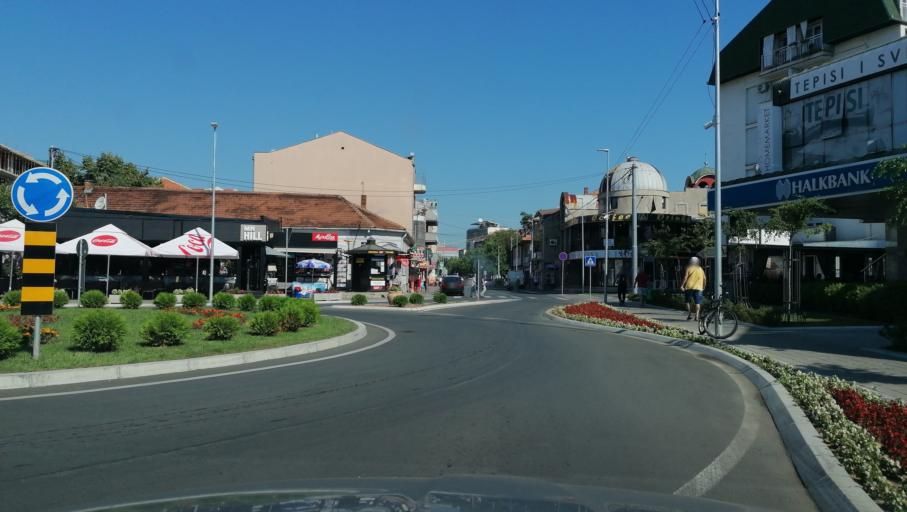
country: RS
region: Central Serbia
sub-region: Rasinski Okrug
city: Krusevac
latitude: 43.5778
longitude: 21.3321
